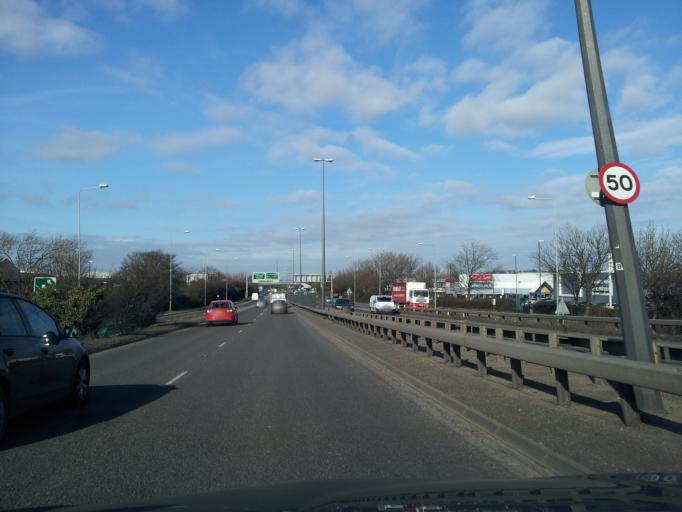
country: GB
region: England
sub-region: Nottingham
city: Nottingham
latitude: 52.9299
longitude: -1.1697
